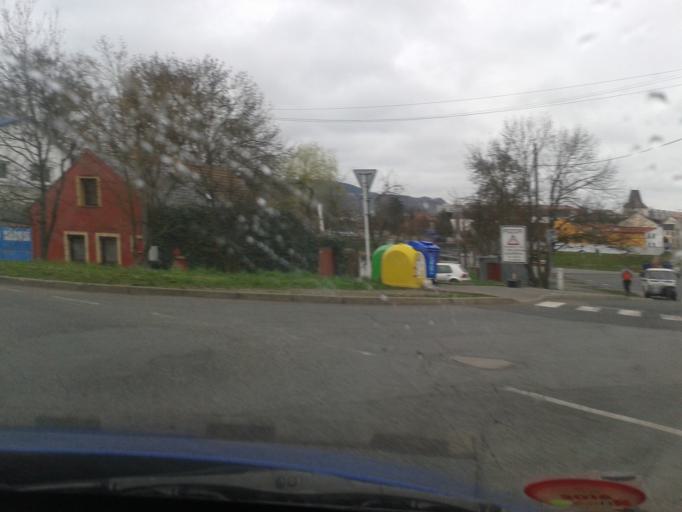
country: CZ
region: Central Bohemia
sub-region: Okres Beroun
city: Beroun
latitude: 49.9662
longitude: 14.0797
